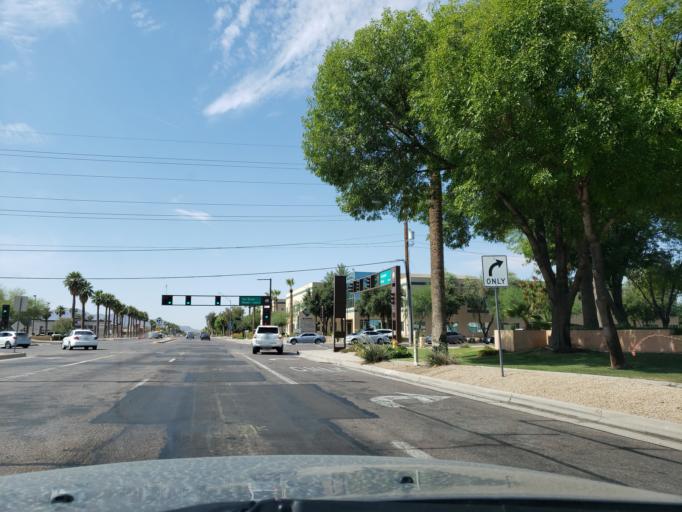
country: US
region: Arizona
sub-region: Maricopa County
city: Goodyear
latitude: 33.4503
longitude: -112.3582
